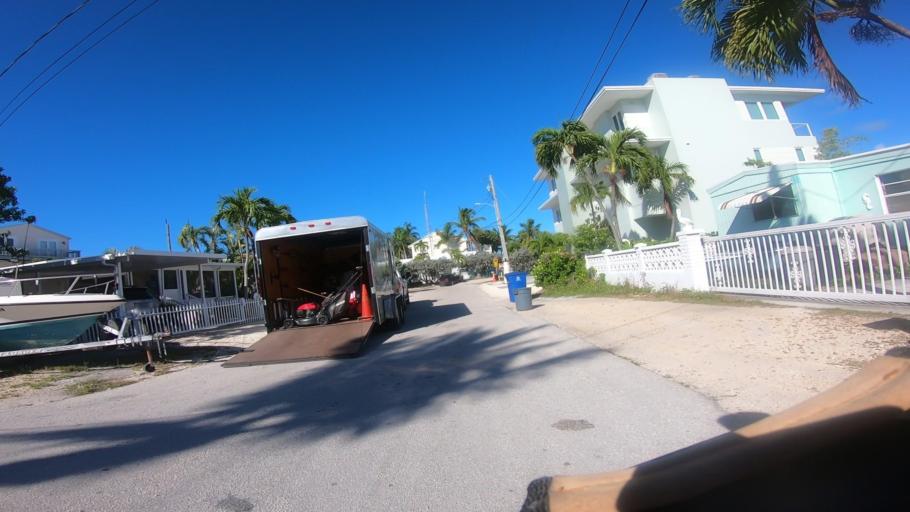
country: US
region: Florida
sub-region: Monroe County
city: Key Largo
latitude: 25.1152
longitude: -80.4253
